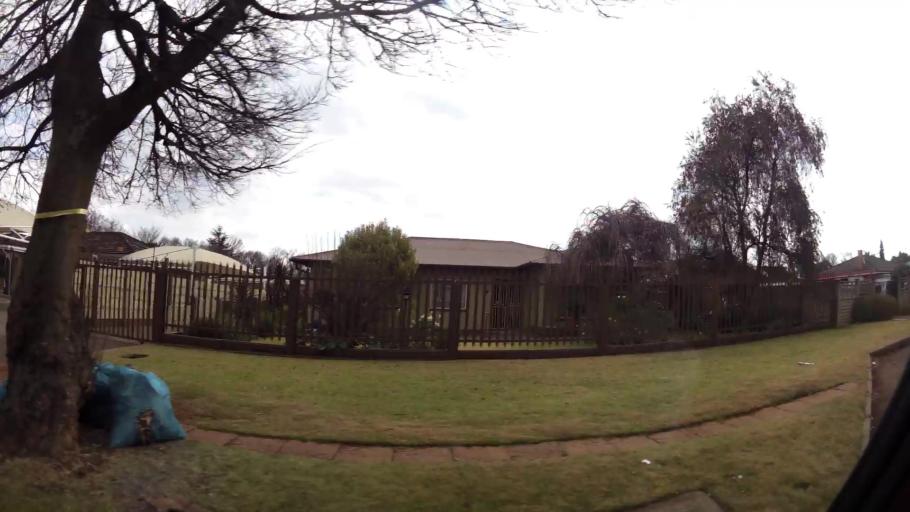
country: ZA
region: Gauteng
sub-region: Sedibeng District Municipality
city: Vanderbijlpark
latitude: -26.6990
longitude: 27.8226
